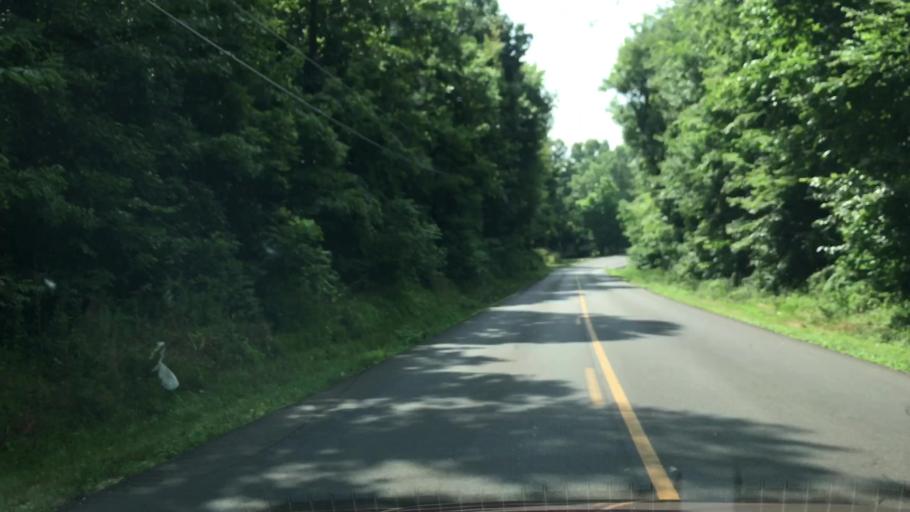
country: US
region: Kentucky
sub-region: Barren County
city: Glasgow
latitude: 36.9874
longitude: -85.9062
